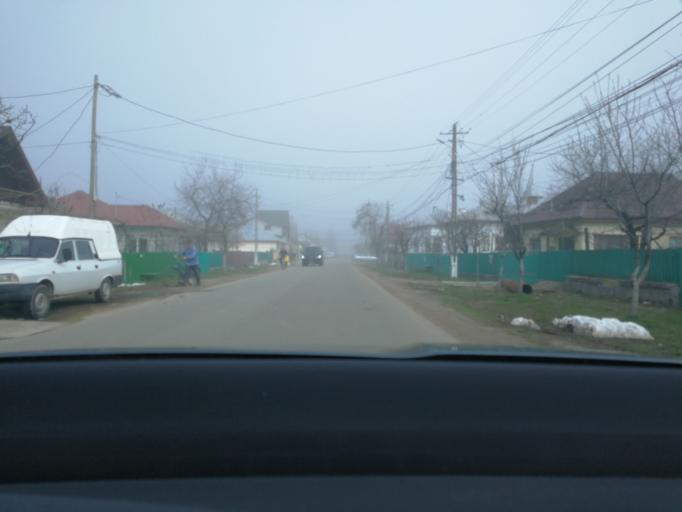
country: RO
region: Prahova
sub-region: Comuna Magureni
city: Lunca Prahovei
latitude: 45.0411
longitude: 25.7531
